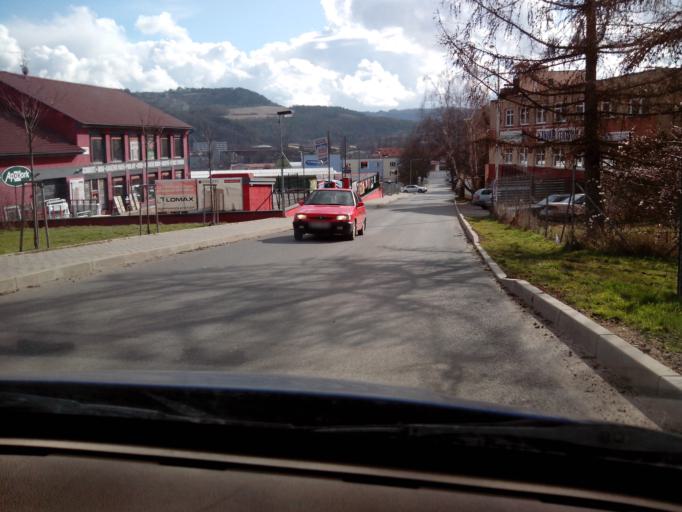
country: CZ
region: Central Bohemia
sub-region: Okres Beroun
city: Kraluv Dvur
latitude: 49.9517
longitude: 14.0363
